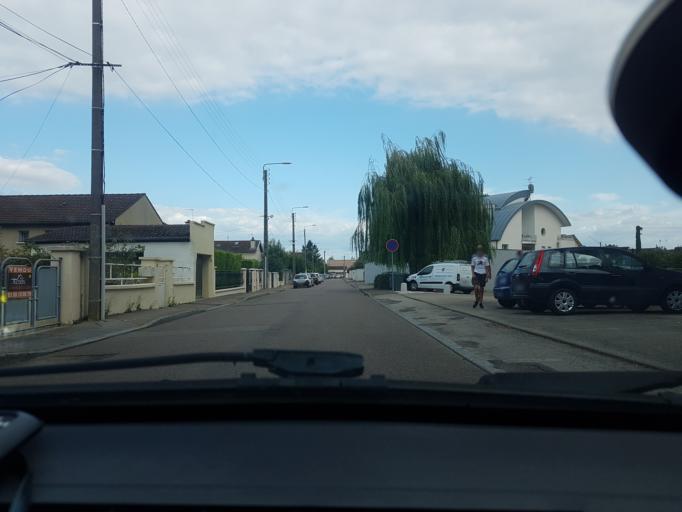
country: FR
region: Bourgogne
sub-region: Departement de la Cote-d'Or
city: Longvic
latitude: 47.3037
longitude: 5.0503
